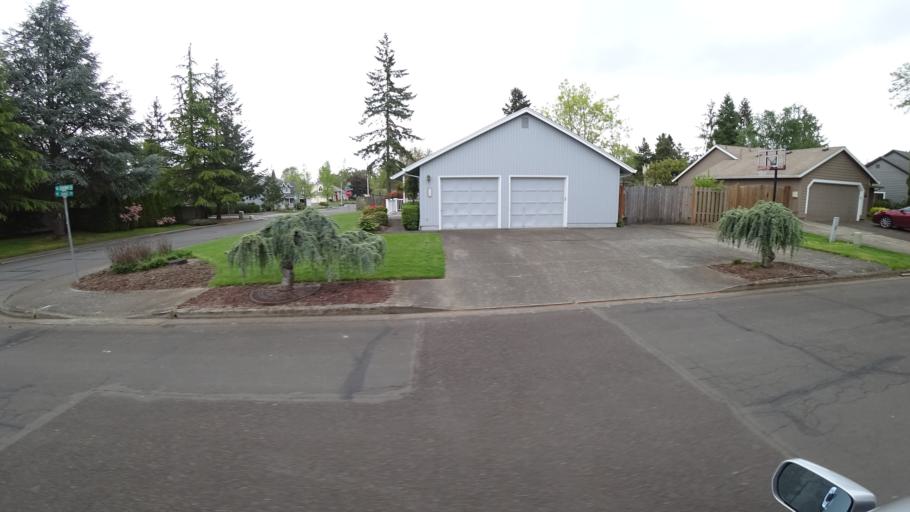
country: US
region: Oregon
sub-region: Washington County
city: Hillsboro
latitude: 45.5387
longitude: -122.9839
